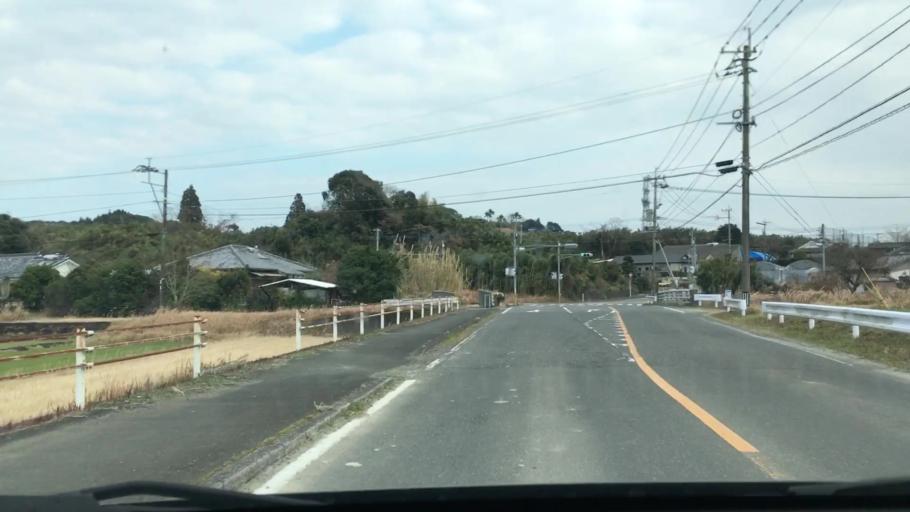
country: JP
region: Miyazaki
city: Kushima
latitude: 31.4679
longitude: 131.2139
